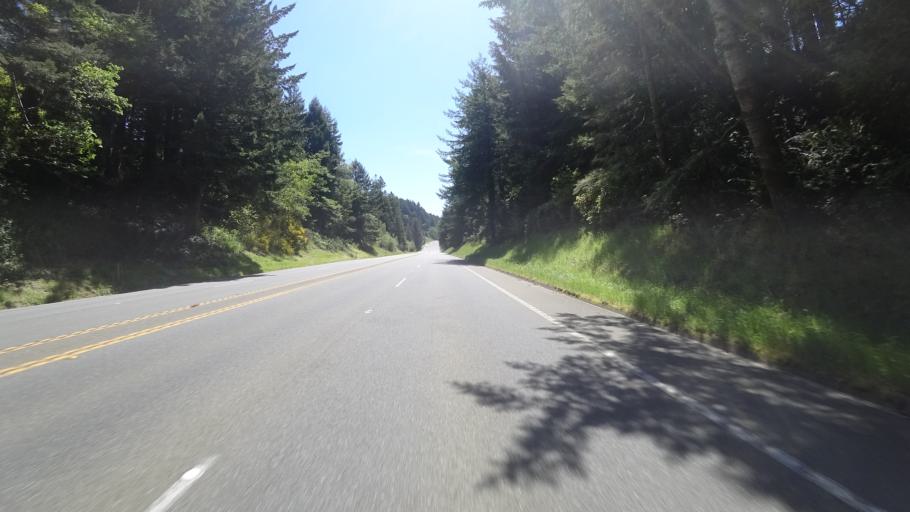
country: US
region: California
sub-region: Humboldt County
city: Westhaven-Moonstone
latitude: 41.0477
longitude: -124.1196
